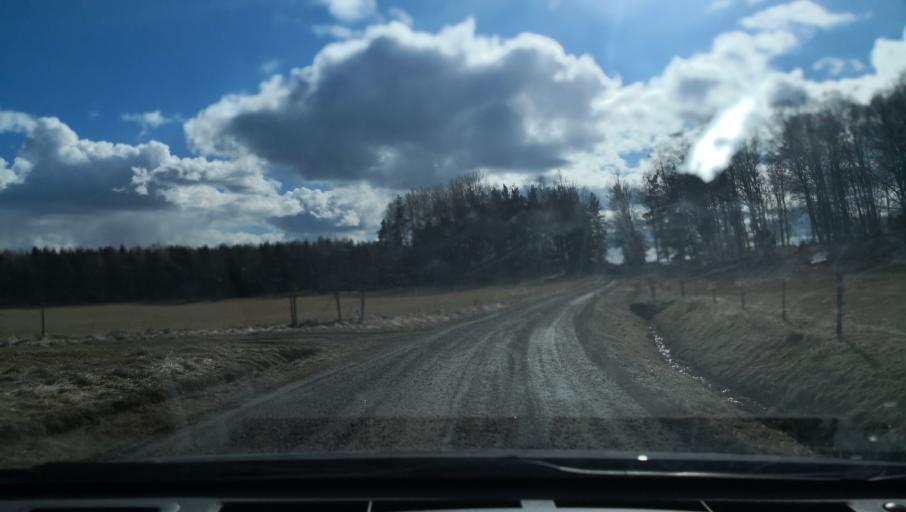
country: SE
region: OErebro
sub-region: Lindesbergs Kommun
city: Fellingsbro
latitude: 59.4158
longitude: 15.6789
